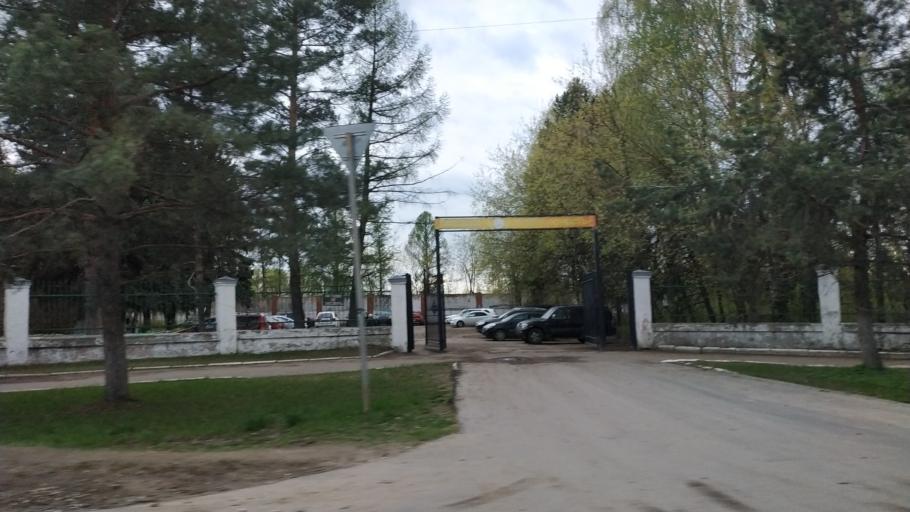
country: RU
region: Moskovskaya
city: Pavlovskiy Posad
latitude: 55.7724
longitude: 38.6879
